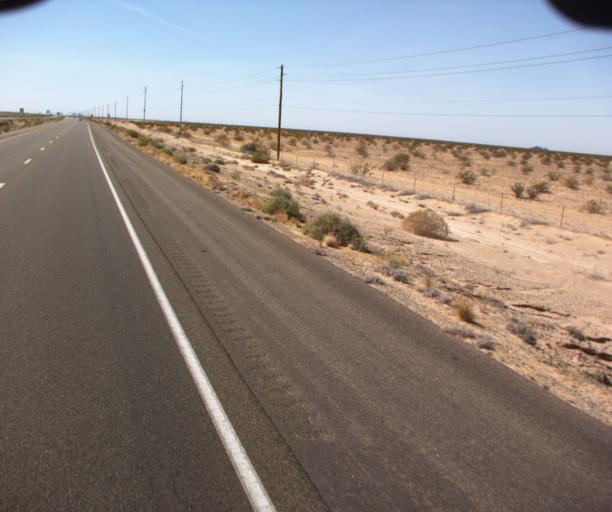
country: MX
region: Sonora
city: San Luis Rio Colorado
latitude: 32.4948
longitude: -114.6898
